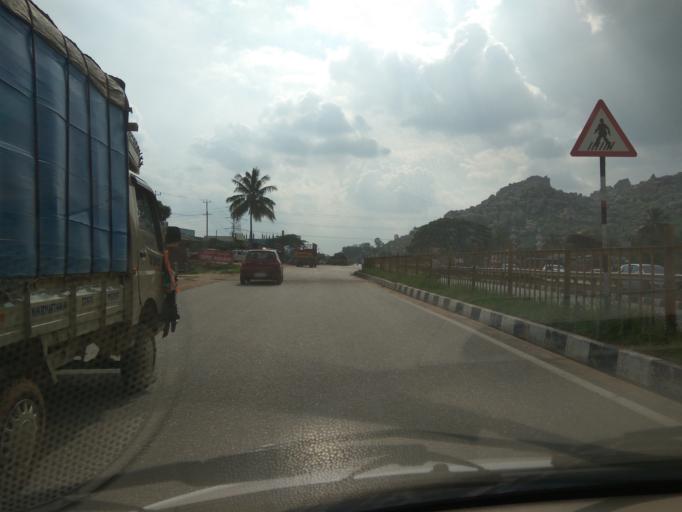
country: IN
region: Karnataka
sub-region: Kolar
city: Kolar
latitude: 13.1229
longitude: 78.1061
